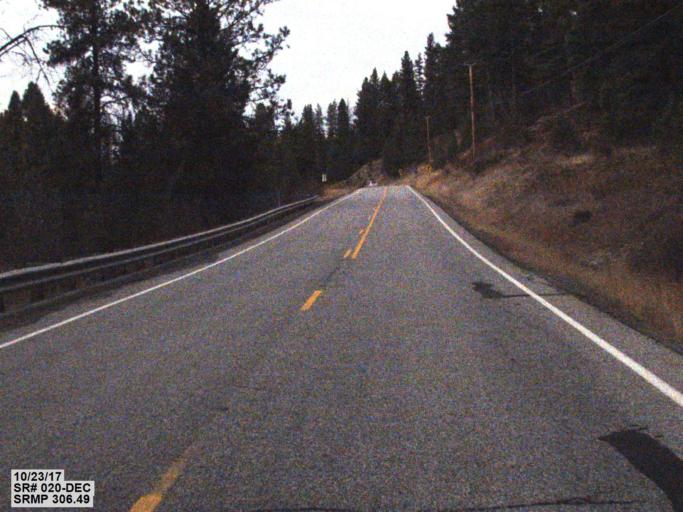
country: US
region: Washington
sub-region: Ferry County
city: Republic
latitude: 48.6346
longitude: -118.6772
